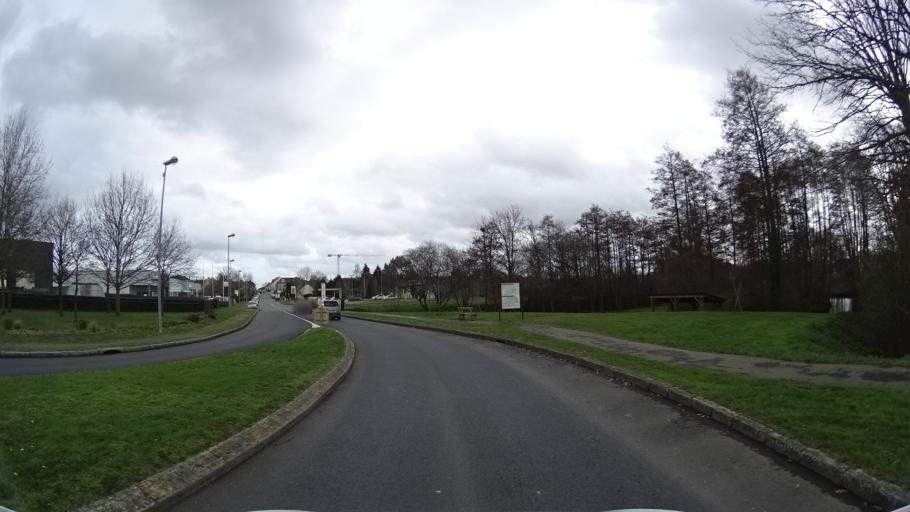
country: FR
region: Brittany
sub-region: Departement d'Ille-et-Vilaine
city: Saint-Gilles
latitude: 48.1568
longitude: -1.8343
